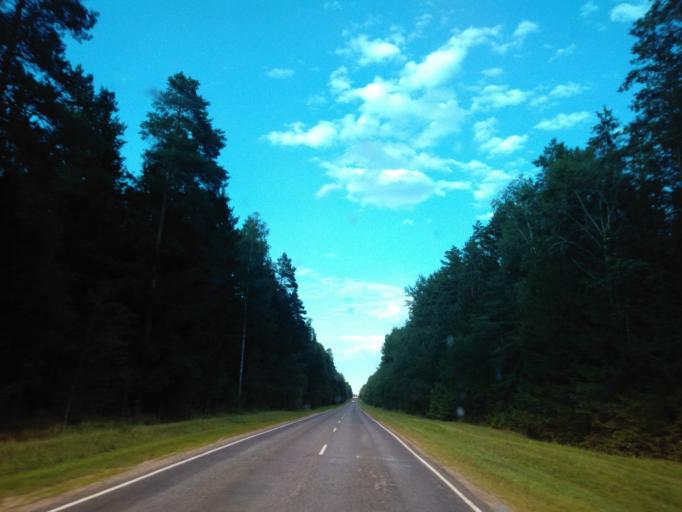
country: BY
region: Minsk
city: Uzda
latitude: 53.4284
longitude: 27.4554
